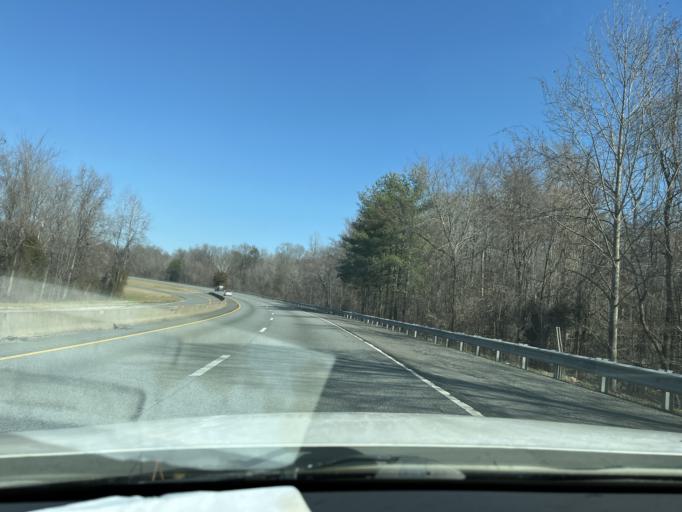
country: US
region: North Carolina
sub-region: Guilford County
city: Jamestown
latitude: 35.9850
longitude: -79.8820
